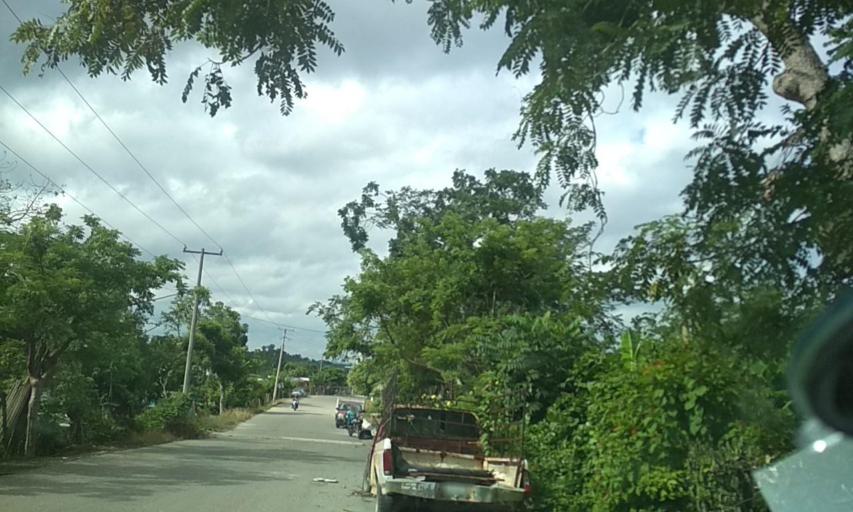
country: MX
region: Veracruz
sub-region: Papantla
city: Polutla
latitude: 20.5403
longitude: -97.2485
